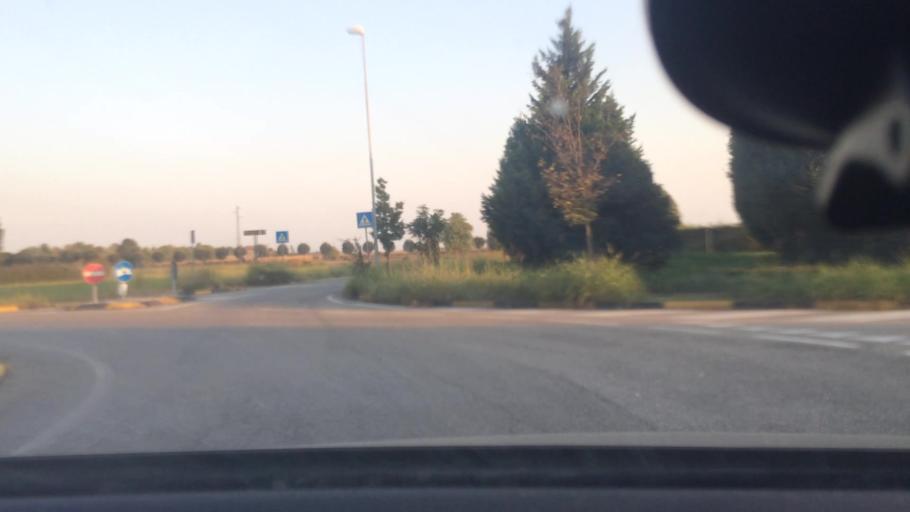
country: IT
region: Lombardy
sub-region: Provincia di Bergamo
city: Brusaporto
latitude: 45.6653
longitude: 9.7489
